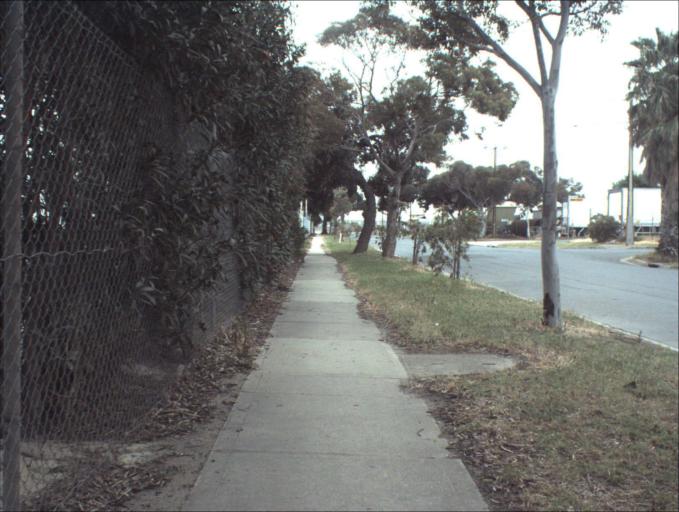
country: AU
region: South Australia
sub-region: Port Adelaide Enfield
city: Enfield
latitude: -34.8372
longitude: 138.5861
